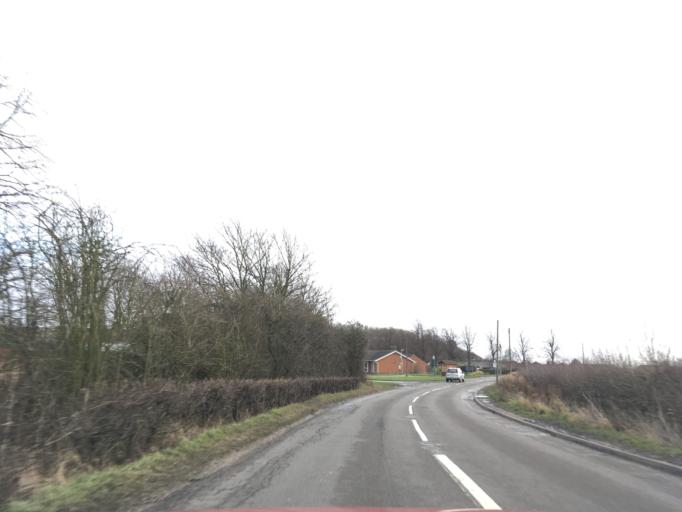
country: GB
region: England
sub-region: Nottinghamshire
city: East Leake
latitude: 52.8434
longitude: -1.1823
